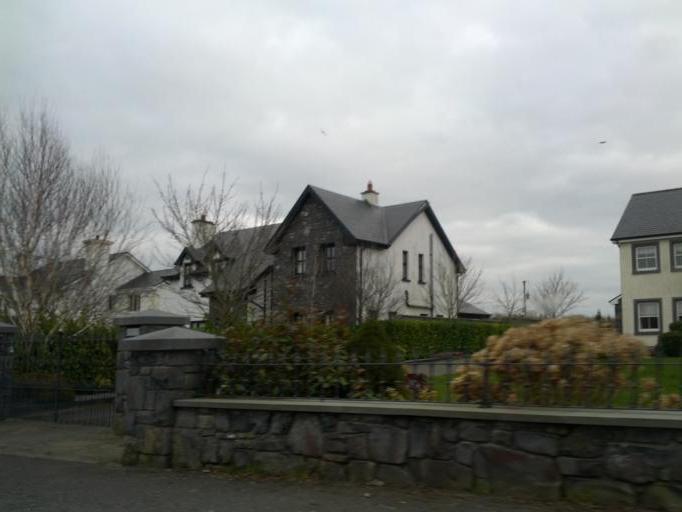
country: IE
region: Connaught
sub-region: County Galway
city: Oranmore
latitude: 53.2227
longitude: -8.8840
